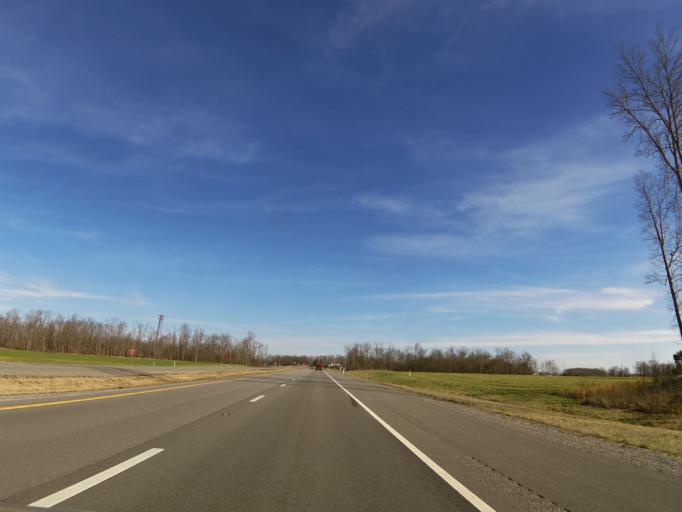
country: US
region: Tennessee
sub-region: Cannon County
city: Woodbury
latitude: 35.7381
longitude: -85.9376
